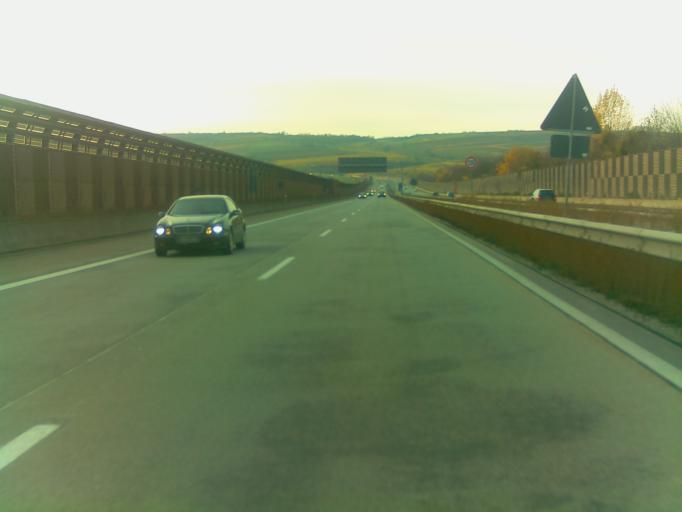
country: DE
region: Rheinland-Pfalz
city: Grunstadt
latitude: 49.5533
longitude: 8.1714
